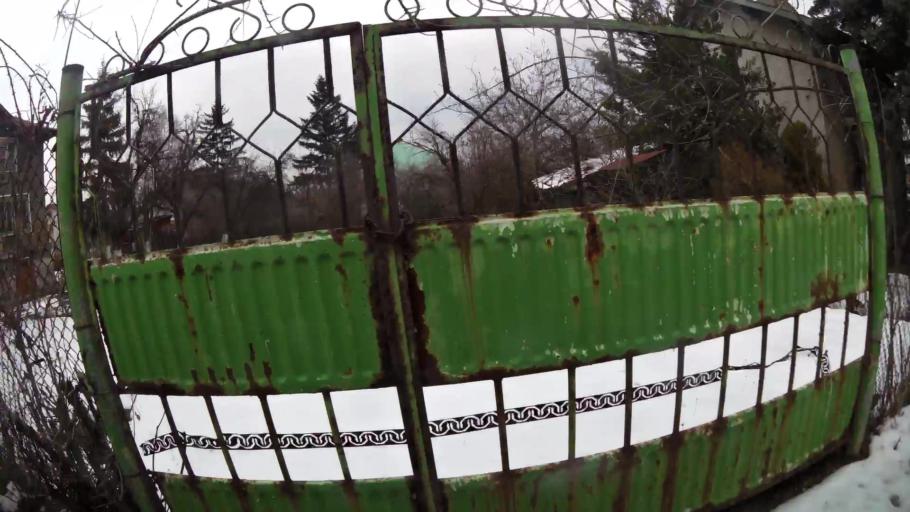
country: BG
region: Sofiya
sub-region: Obshtina Bozhurishte
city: Bozhurishte
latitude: 42.6726
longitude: 23.2351
